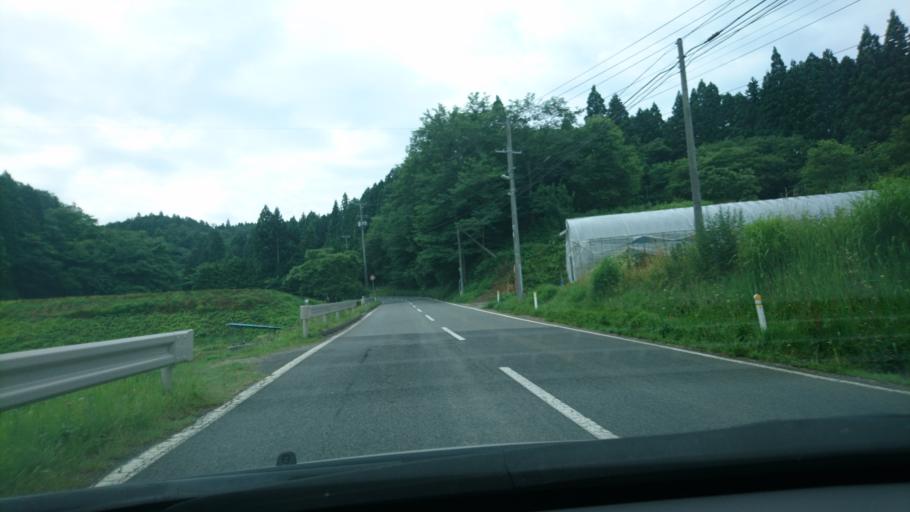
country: JP
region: Iwate
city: Ichinoseki
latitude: 38.8853
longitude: 141.4246
